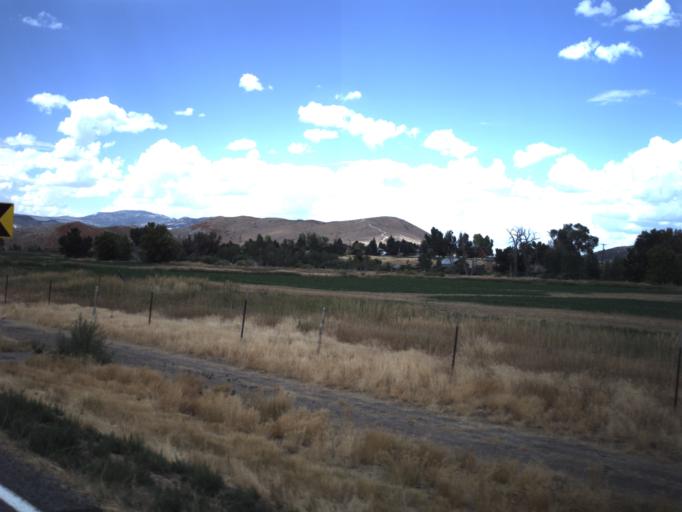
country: US
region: Utah
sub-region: Sanpete County
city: Centerfield
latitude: 39.1231
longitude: -111.7159
